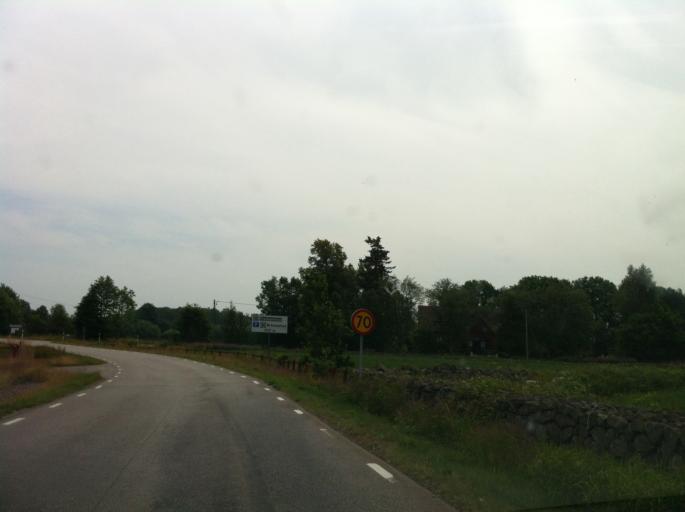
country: SE
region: Kalmar
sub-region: Torsas Kommun
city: Torsas
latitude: 56.3216
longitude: 16.0335
